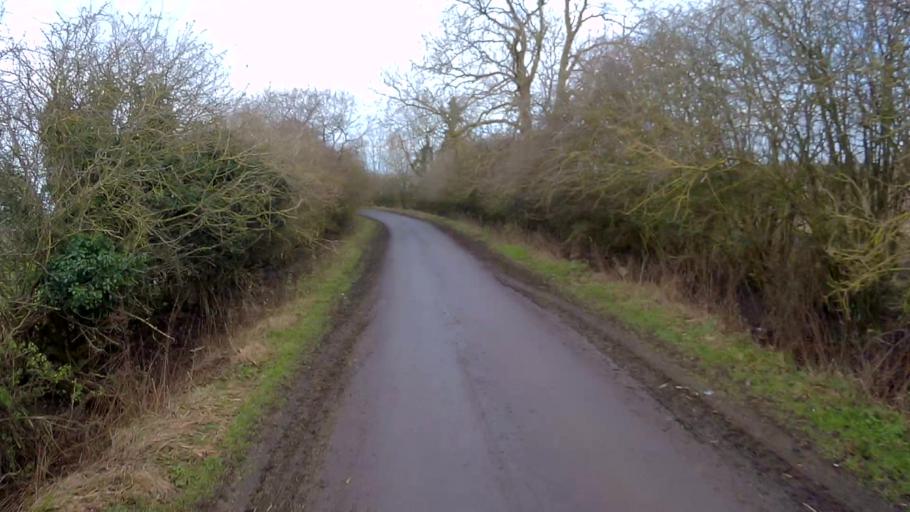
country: GB
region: England
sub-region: Lincolnshire
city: Bourne
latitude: 52.8143
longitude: -0.4362
